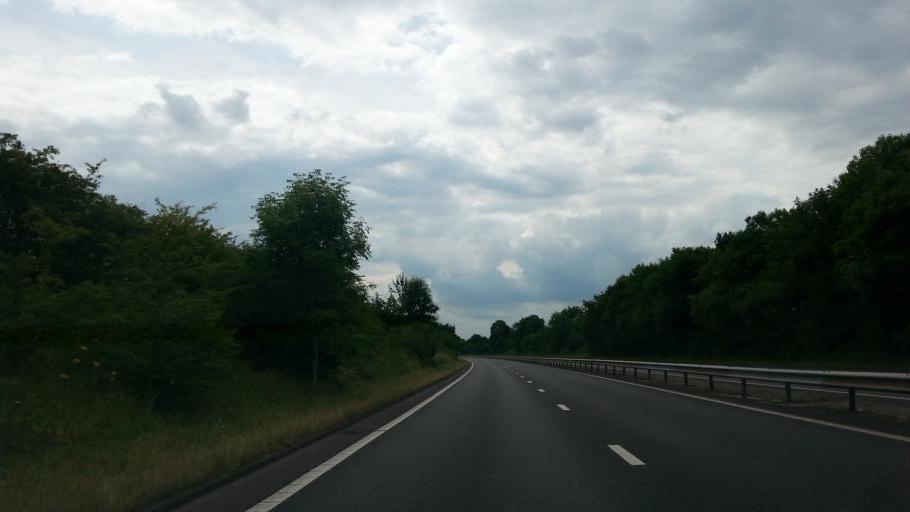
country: GB
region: England
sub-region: Warwickshire
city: Curdworth
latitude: 52.5412
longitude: -1.7784
